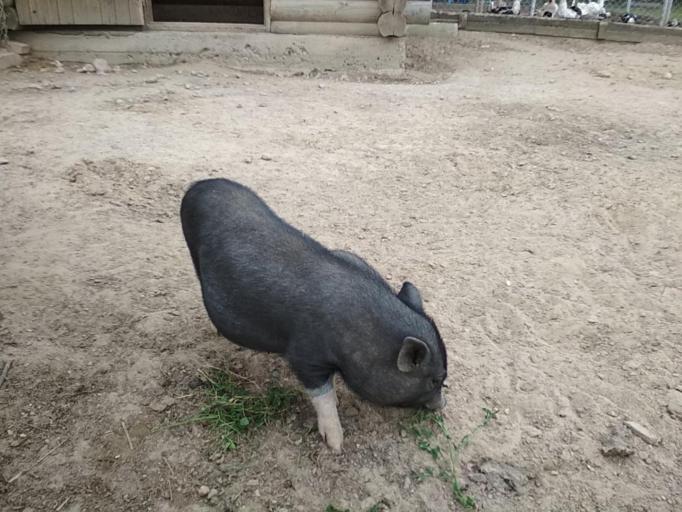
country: BY
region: Minsk
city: Dukora
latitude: 53.6759
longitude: 27.9679
